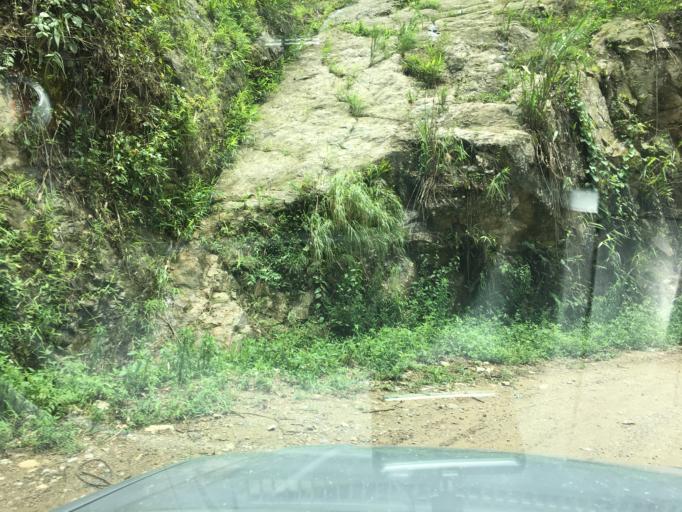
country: VN
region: Yen Bai
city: Son Thinh
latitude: 21.6836
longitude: 104.5713
